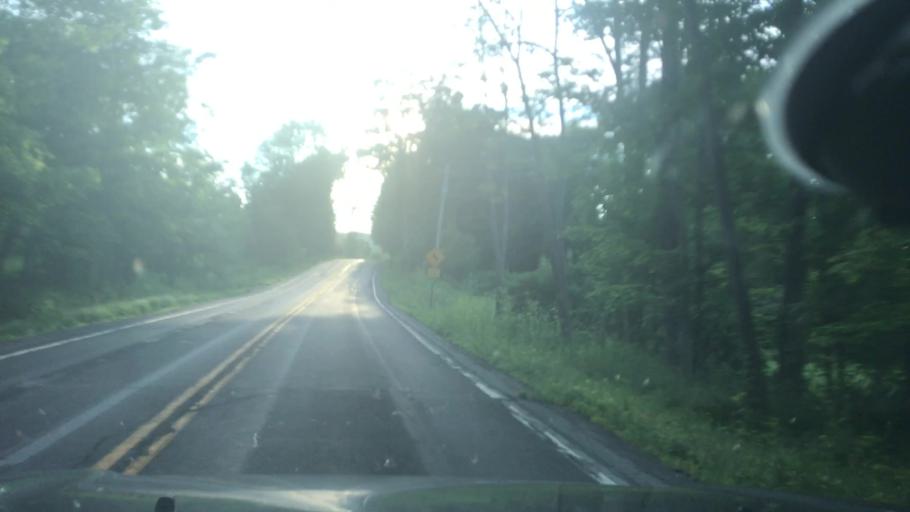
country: US
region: New York
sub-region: Otsego County
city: Unadilla
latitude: 42.3394
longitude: -75.2536
